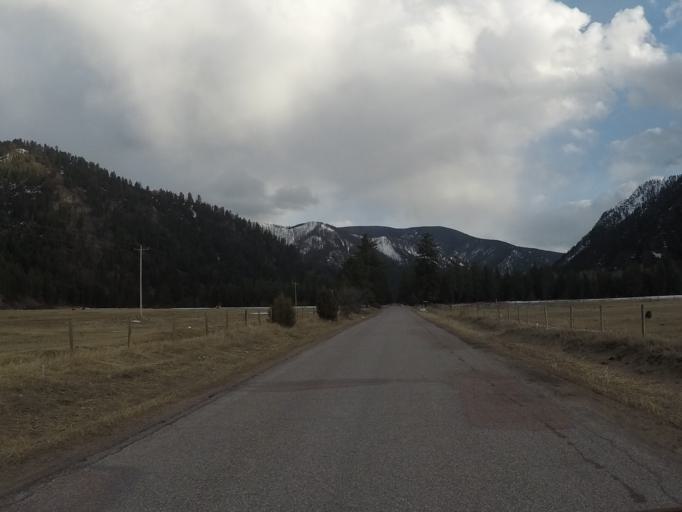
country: US
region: Montana
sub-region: Missoula County
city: Clinton
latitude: 46.6541
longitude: -113.6559
